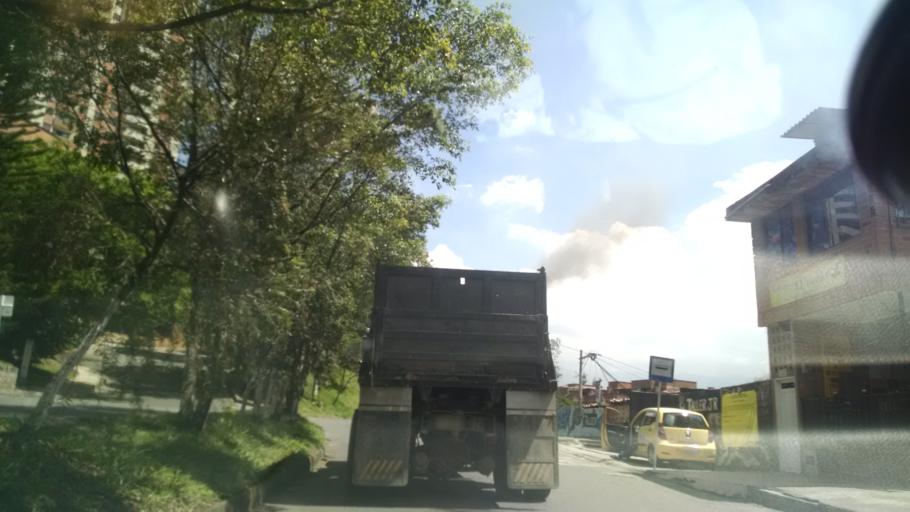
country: CO
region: Antioquia
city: Itagui
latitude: 6.2150
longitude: -75.6014
